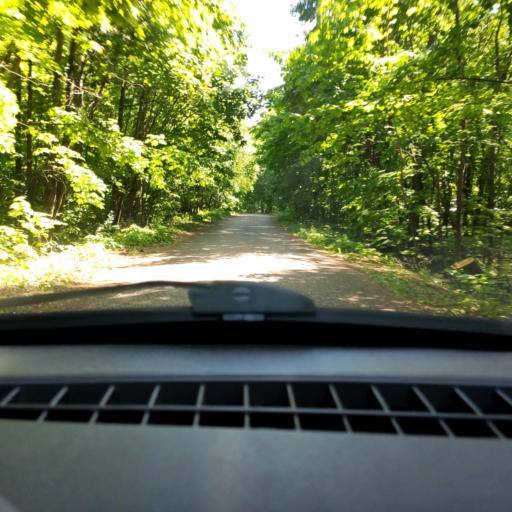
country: RU
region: Bashkortostan
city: Kabakovo
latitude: 54.4295
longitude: 55.9157
